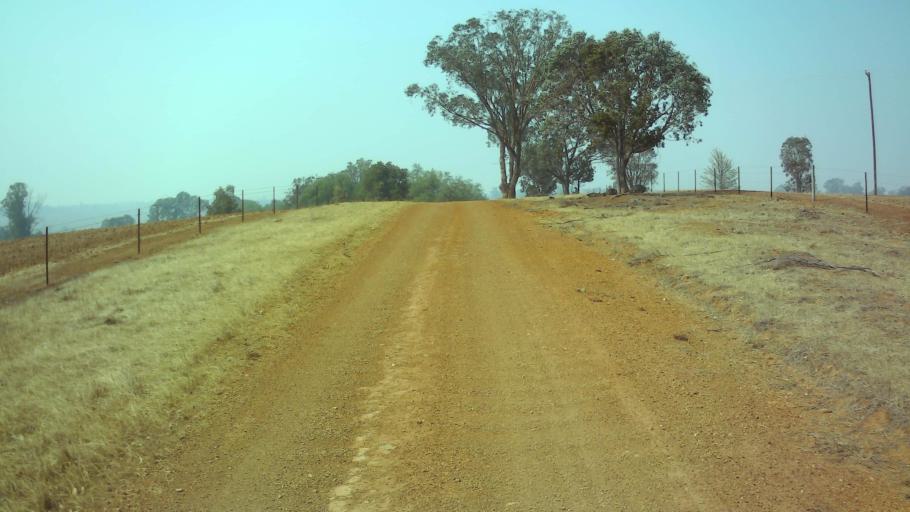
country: AU
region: New South Wales
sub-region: Weddin
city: Grenfell
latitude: -33.9278
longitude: 148.2069
